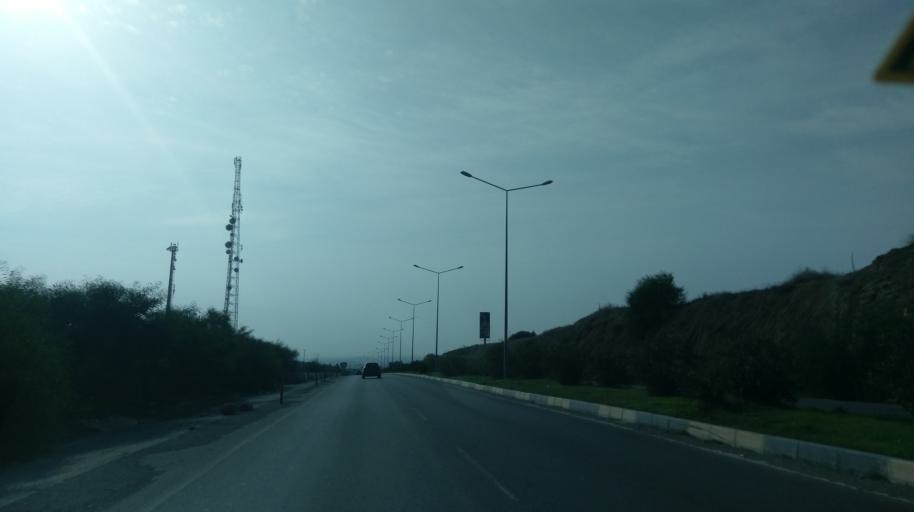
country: CY
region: Lefkosia
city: Nicosia
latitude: 35.2329
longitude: 33.3119
